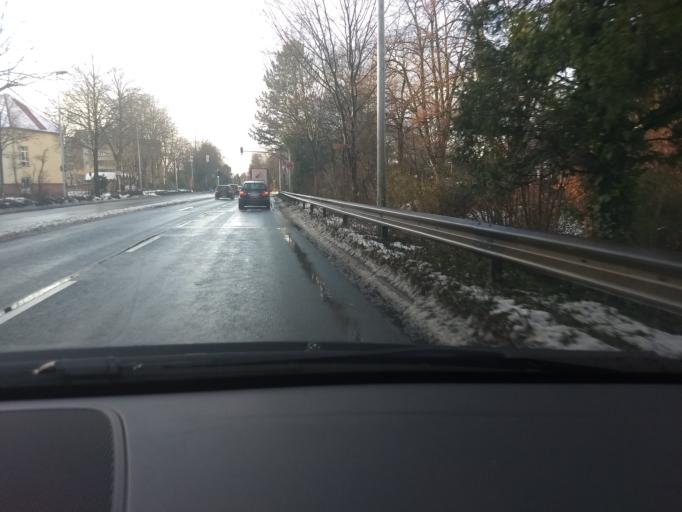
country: DE
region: Lower Saxony
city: Nordhorn
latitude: 52.4408
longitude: 7.0740
